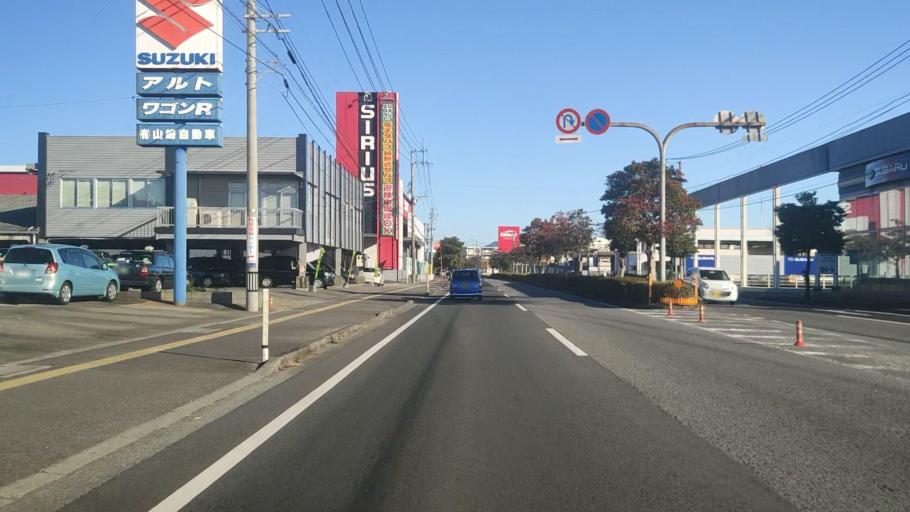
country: JP
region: Miyazaki
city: Nobeoka
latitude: 32.5666
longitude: 131.6828
